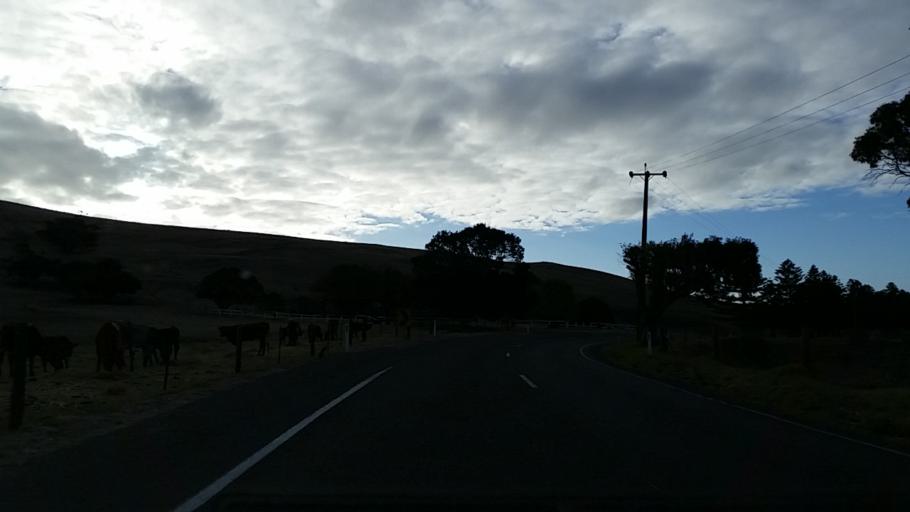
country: AU
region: South Australia
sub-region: Yankalilla
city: Normanville
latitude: -35.5325
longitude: 138.1927
